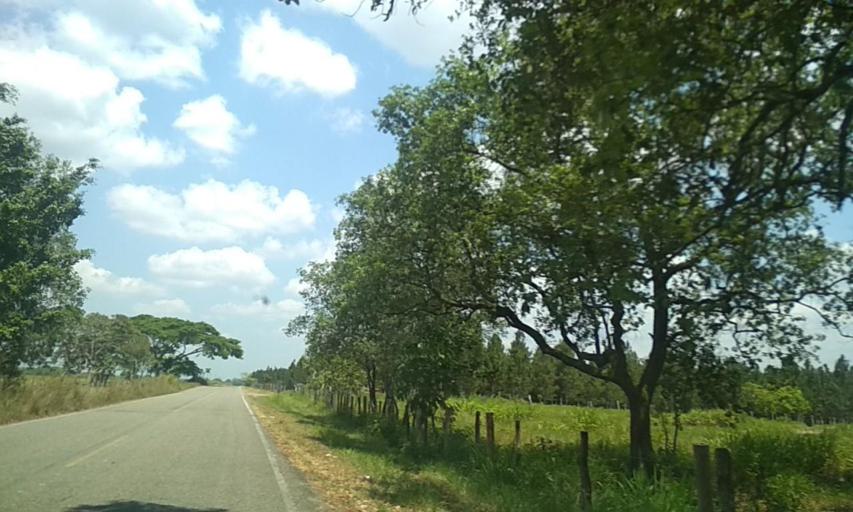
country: MX
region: Tabasco
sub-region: Huimanguillo
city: Huapacal 1ra. Seccion
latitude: 17.7562
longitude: -93.7688
